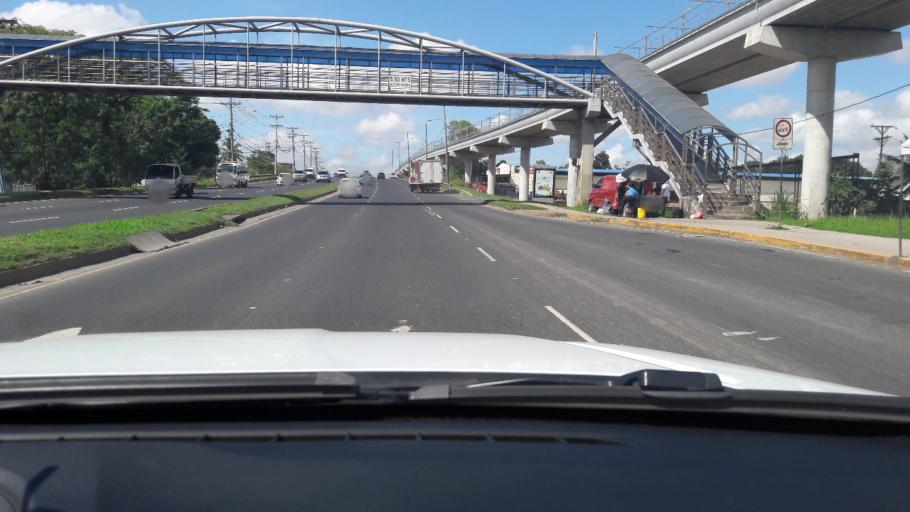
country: PA
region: Panama
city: Tocumen
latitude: 9.0675
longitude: -79.4109
